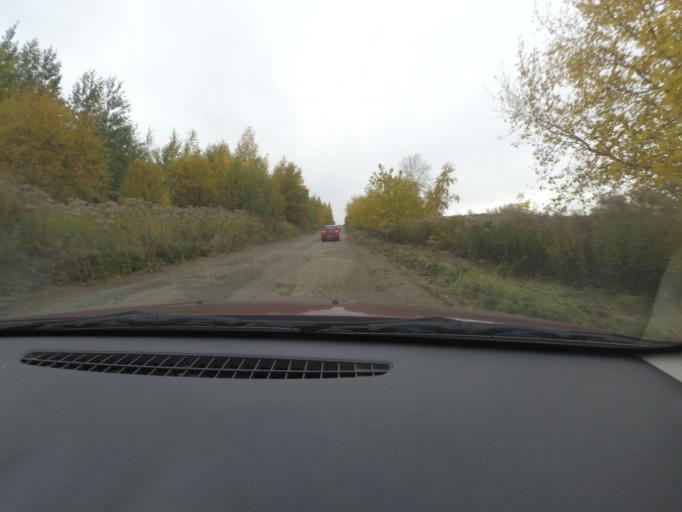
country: RU
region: Nizjnij Novgorod
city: Afonino
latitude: 56.2653
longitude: 44.0402
